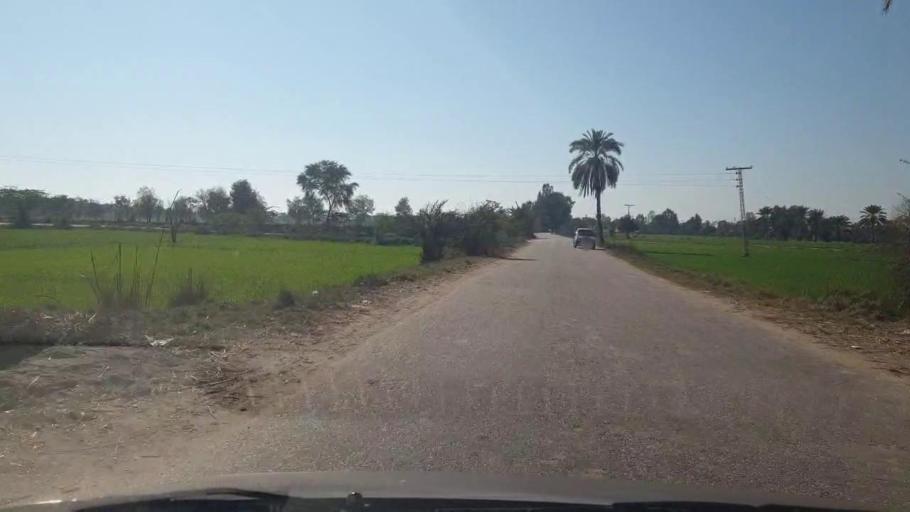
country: PK
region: Sindh
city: Bozdar
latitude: 27.1003
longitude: 68.6301
